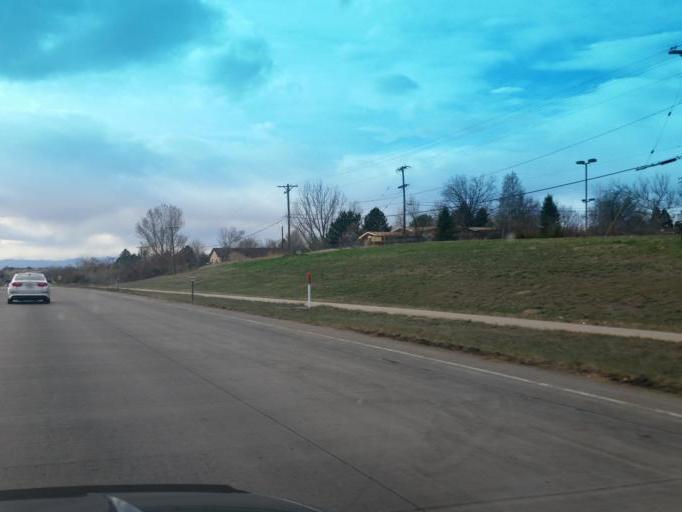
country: US
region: Colorado
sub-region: Weld County
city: Greeley
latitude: 40.3922
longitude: -104.7594
